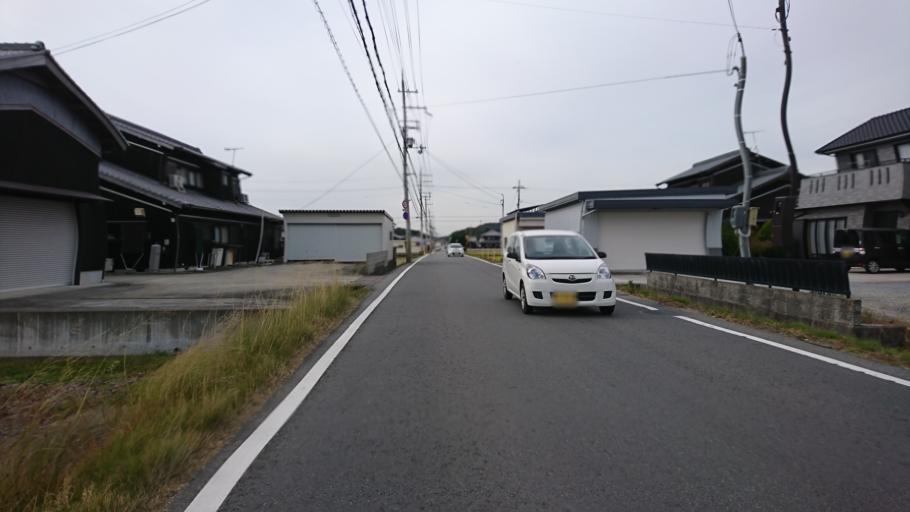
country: JP
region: Hyogo
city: Ono
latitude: 34.7852
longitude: 134.9069
